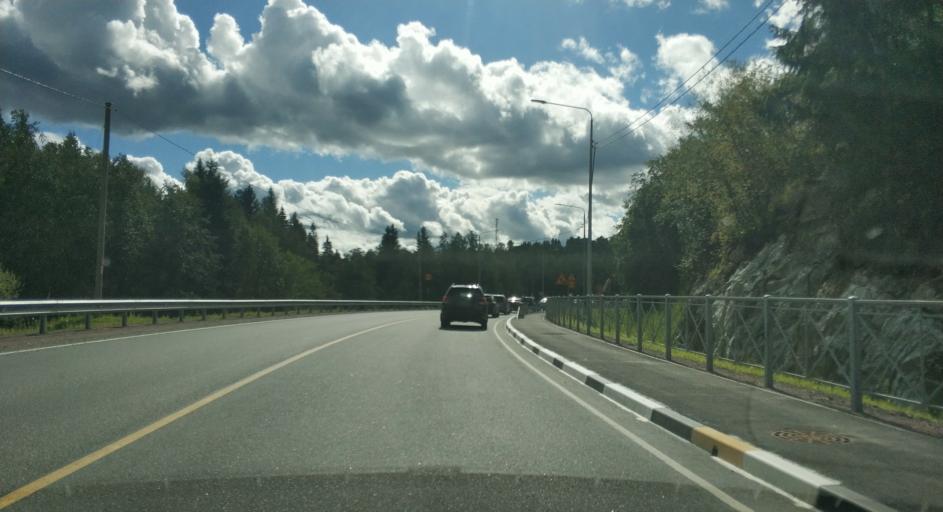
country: RU
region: Republic of Karelia
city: Ruskeala
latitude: 61.9392
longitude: 30.5918
